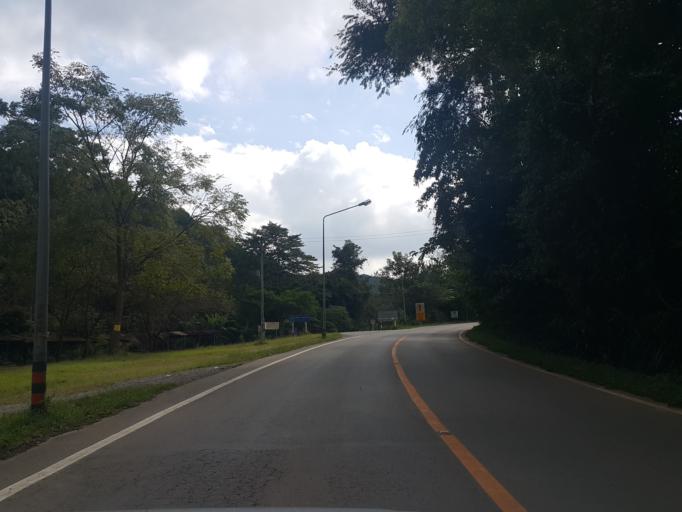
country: TH
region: Chiang Mai
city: Mae Chaem
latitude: 18.5286
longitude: 98.5231
